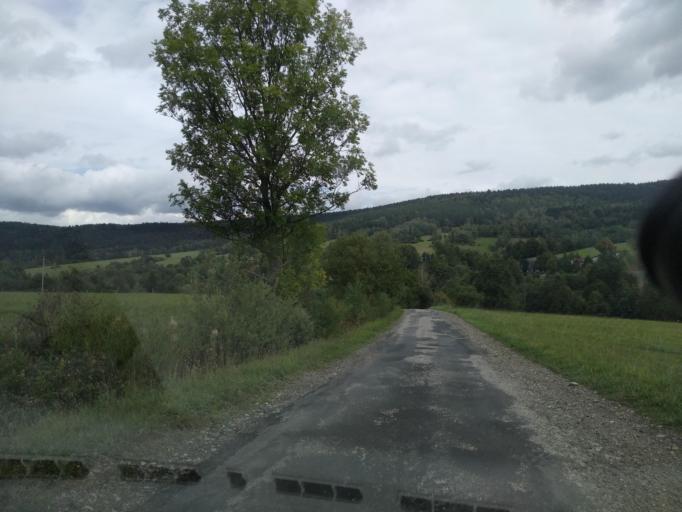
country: PL
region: Lesser Poland Voivodeship
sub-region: Powiat gorlicki
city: Uscie Gorlickie
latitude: 49.5458
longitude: 21.1851
